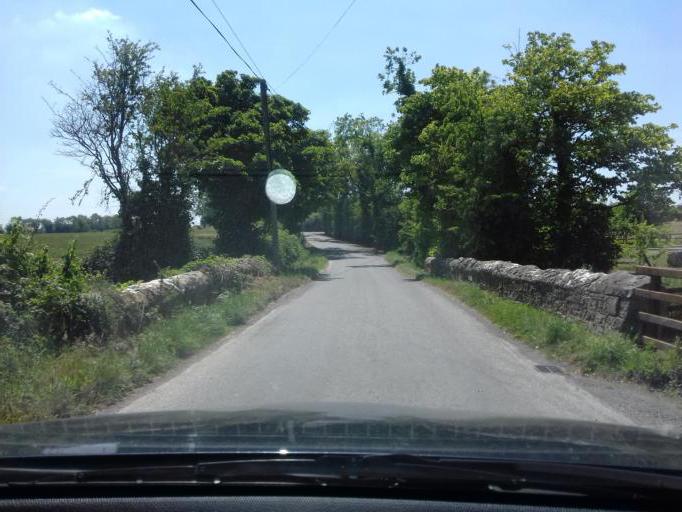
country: IE
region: Leinster
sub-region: Fingal County
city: Swords
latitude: 53.5290
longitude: -6.2525
